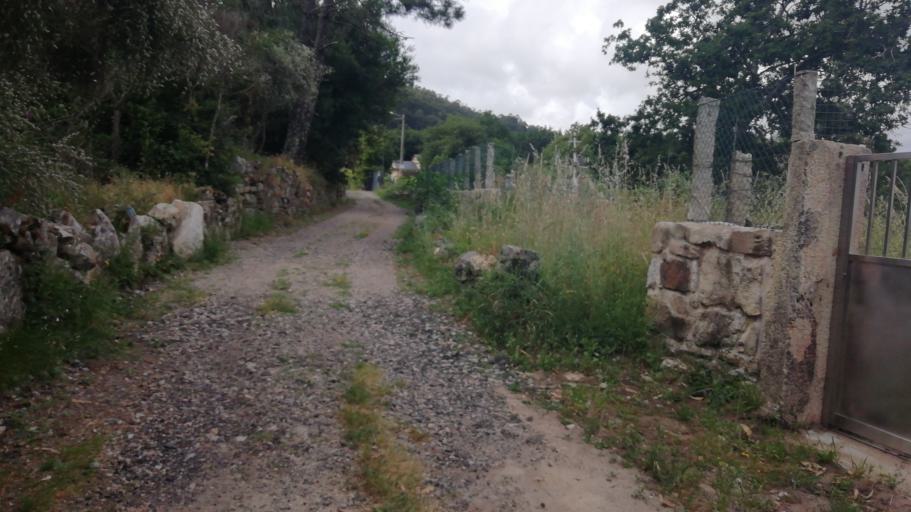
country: ES
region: Galicia
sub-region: Provincia de Pontevedra
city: A Guarda
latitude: 41.8829
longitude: -8.8603
